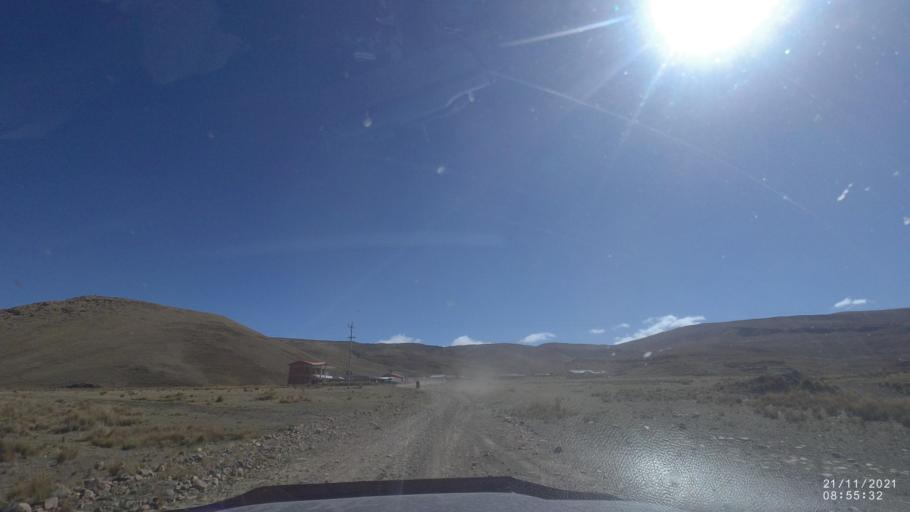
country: BO
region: Cochabamba
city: Cochabamba
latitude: -17.1979
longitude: -66.2459
